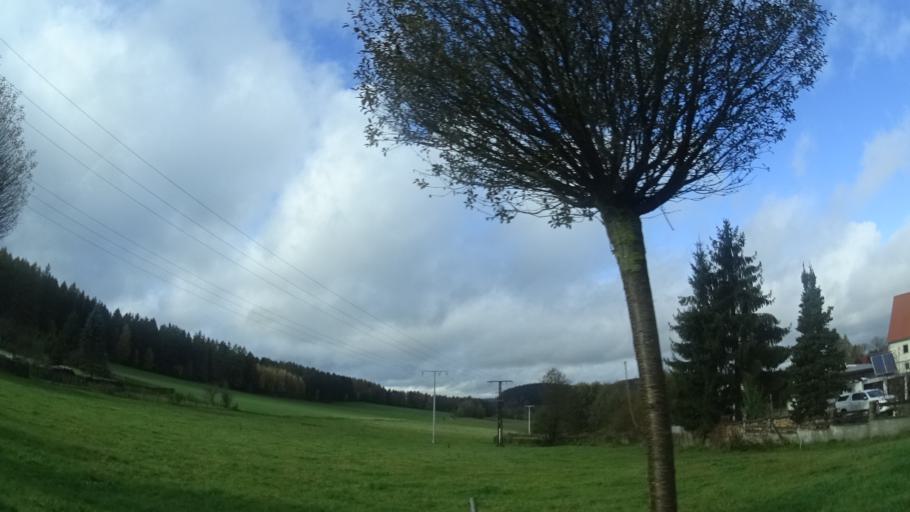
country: DE
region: Thuringia
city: Schleusingen
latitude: 50.4825
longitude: 10.8288
